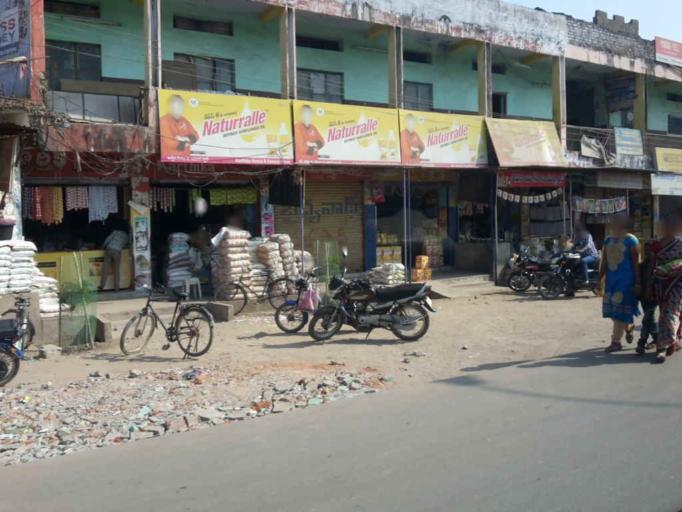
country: IN
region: Telangana
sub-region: Karimnagar
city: Koratla
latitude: 18.8484
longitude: 78.6214
